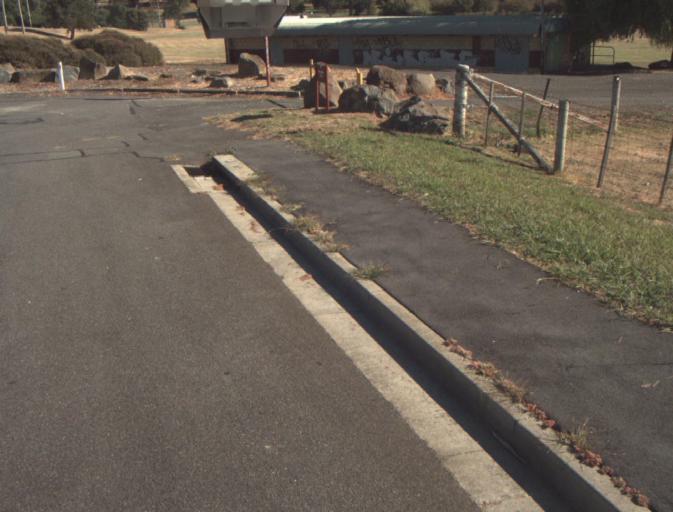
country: AU
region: Tasmania
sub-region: Launceston
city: Newnham
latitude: -41.4010
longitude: 147.1404
